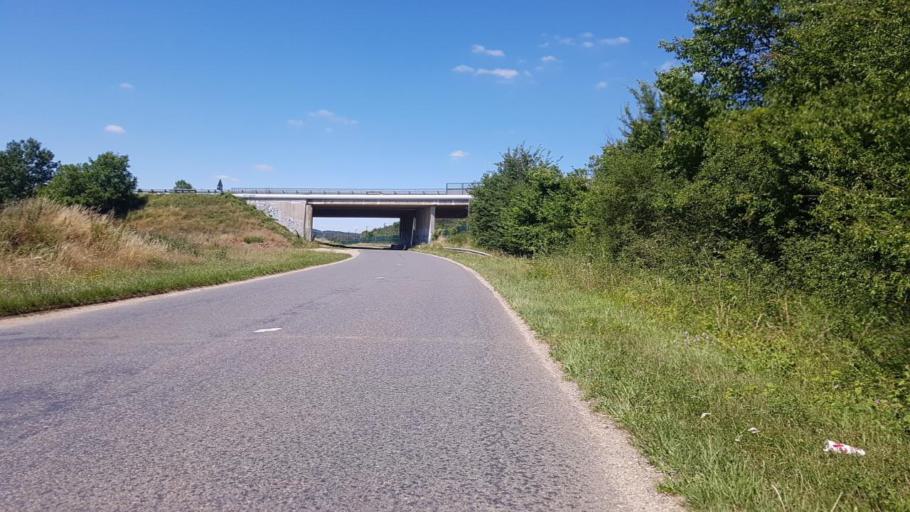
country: FR
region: Ile-de-France
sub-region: Departement de Seine-et-Marne
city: Changis-sur-Marne
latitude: 48.9593
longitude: 3.0527
